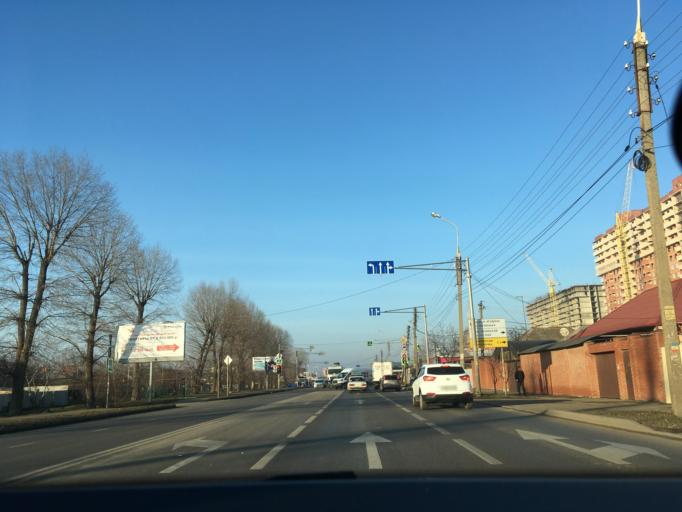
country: RU
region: Krasnodarskiy
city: Krasnodar
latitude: 45.1036
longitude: 39.0129
